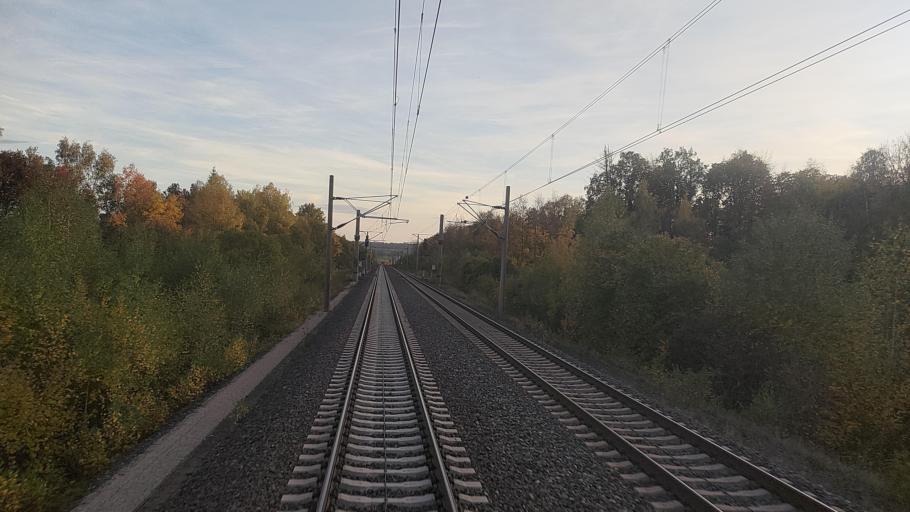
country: DE
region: Lower Saxony
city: Lamspringe
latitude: 51.9245
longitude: 9.9997
